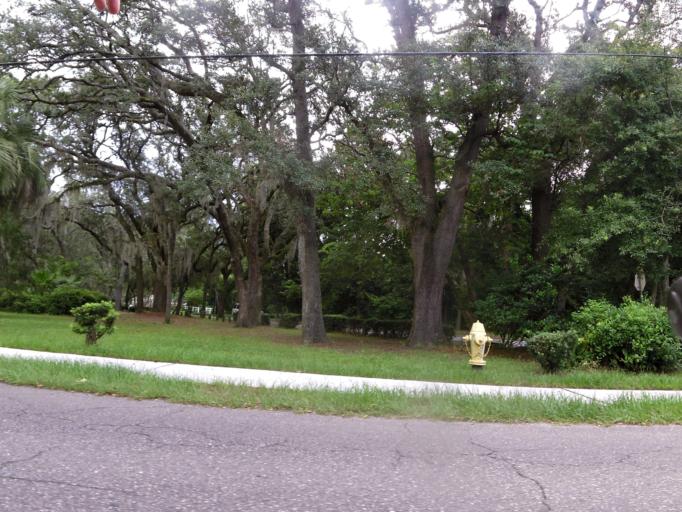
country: US
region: Florida
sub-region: Duval County
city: Jacksonville
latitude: 30.2804
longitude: -81.7135
